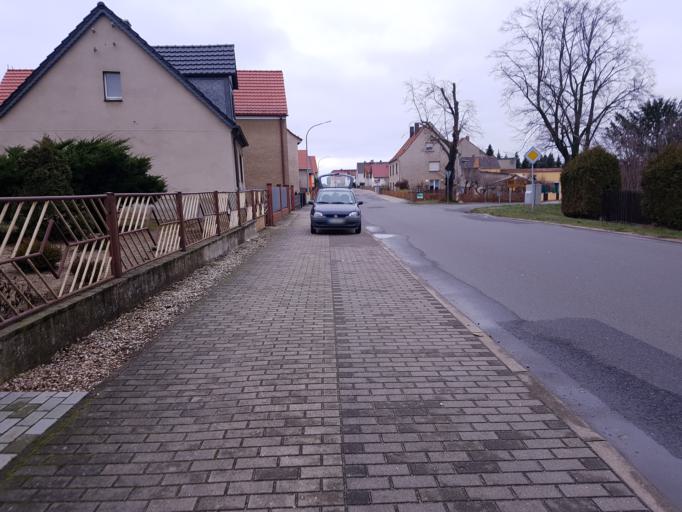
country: DE
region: Brandenburg
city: Groden
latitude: 51.4022
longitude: 13.5793
